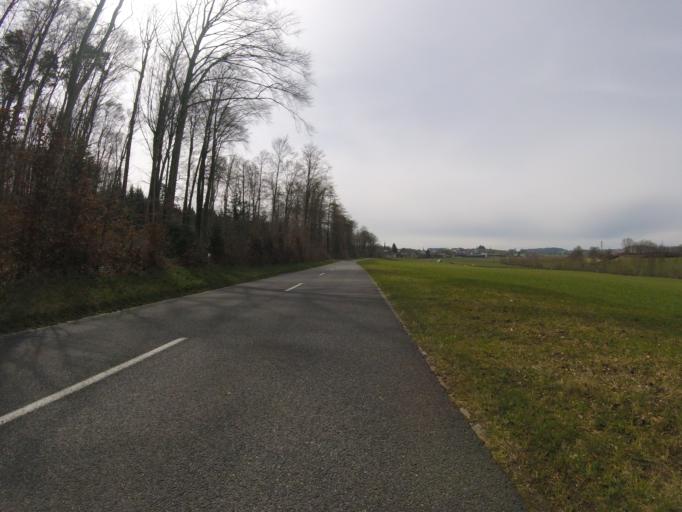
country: CH
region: Fribourg
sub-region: Sense District
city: Bosingen
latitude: 46.8994
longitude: 7.1859
